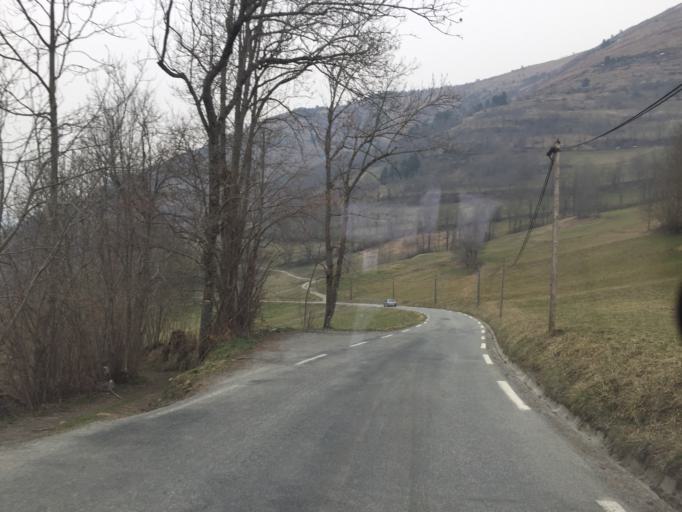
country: FR
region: Midi-Pyrenees
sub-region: Departement des Hautes-Pyrenees
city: Saint-Lary-Soulan
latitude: 42.8113
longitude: 0.3472
